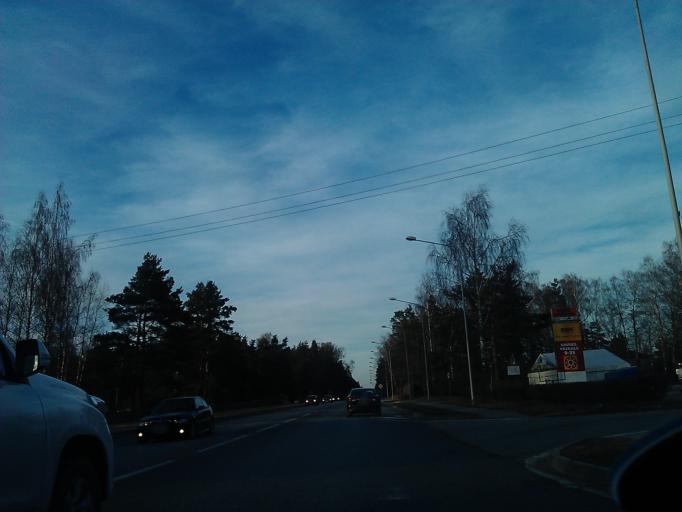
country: LV
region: Adazi
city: Adazi
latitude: 57.0442
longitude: 24.3158
